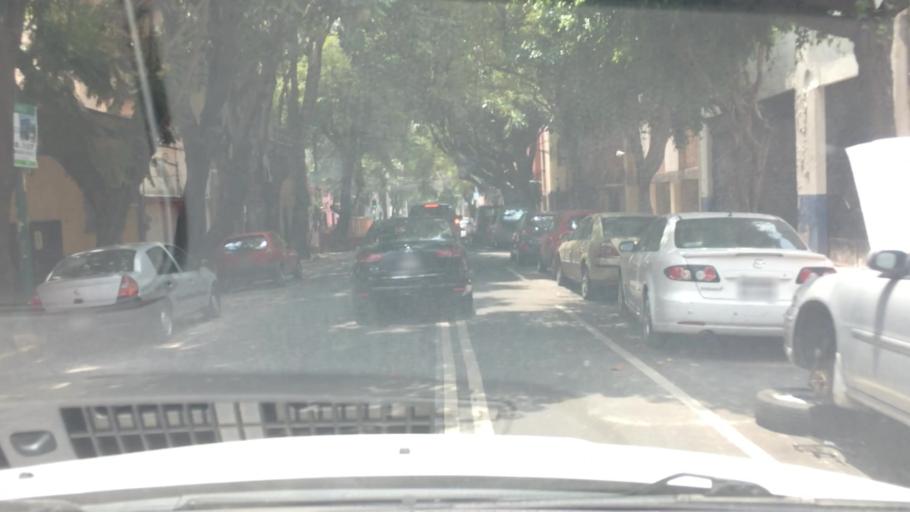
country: MX
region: Mexico City
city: Benito Juarez
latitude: 19.4028
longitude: -99.1761
